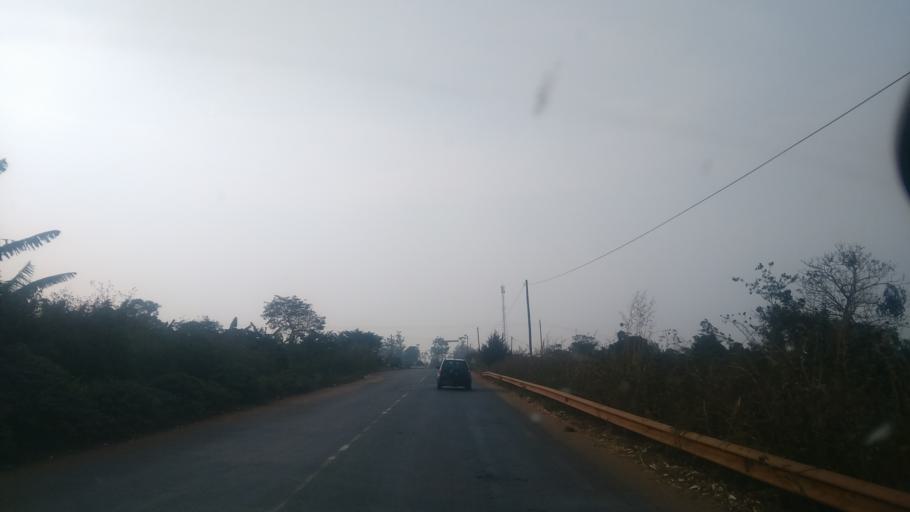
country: CM
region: West
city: Bangangte
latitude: 5.1270
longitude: 10.5798
